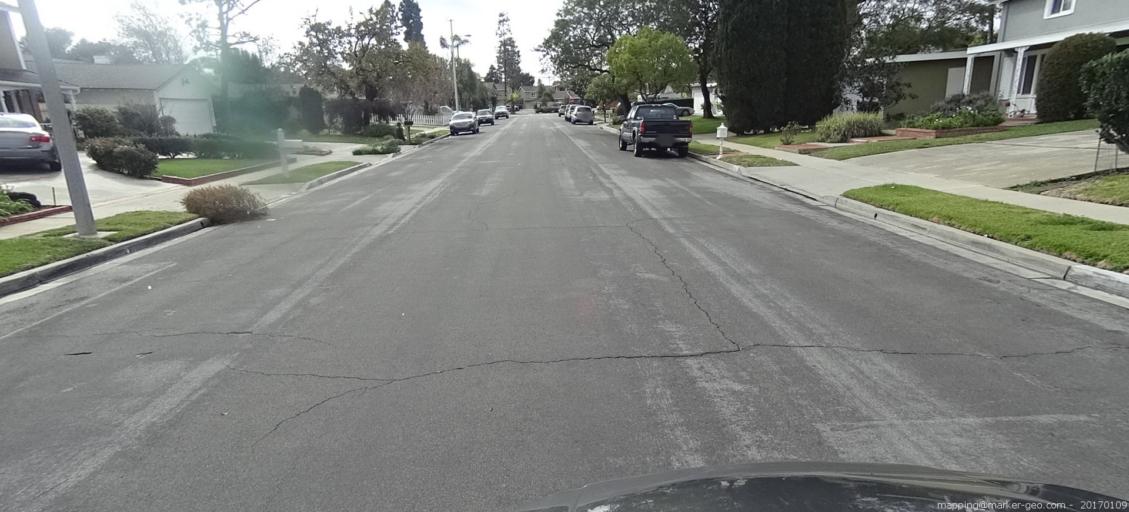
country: US
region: California
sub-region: Orange County
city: Costa Mesa
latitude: 33.6583
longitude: -117.8882
